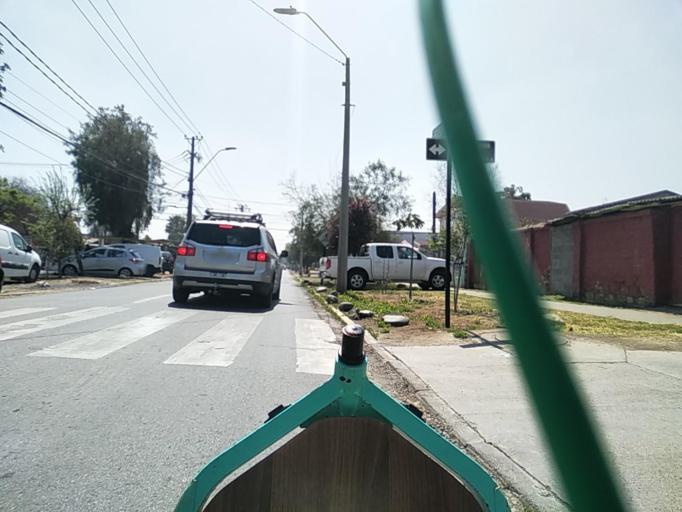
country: CL
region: Santiago Metropolitan
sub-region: Provincia de Santiago
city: Villa Presidente Frei, Nunoa, Santiago, Chile
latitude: -33.5042
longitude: -70.5962
